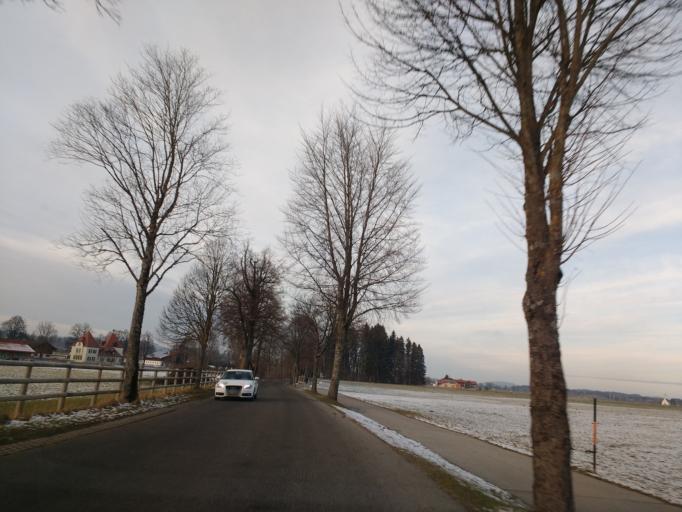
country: DE
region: Bavaria
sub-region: Swabia
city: Schwangau
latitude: 47.5658
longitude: 10.7381
